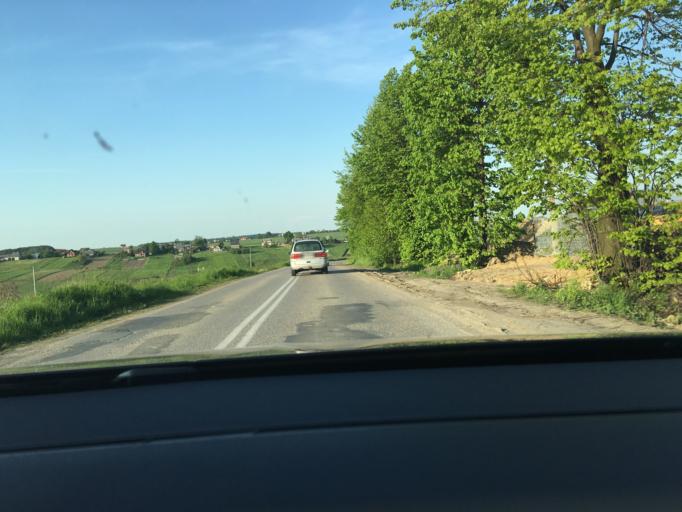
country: PL
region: Lesser Poland Voivodeship
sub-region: Powiat krakowski
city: Jerzmanowice
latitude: 50.2217
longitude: 19.7497
